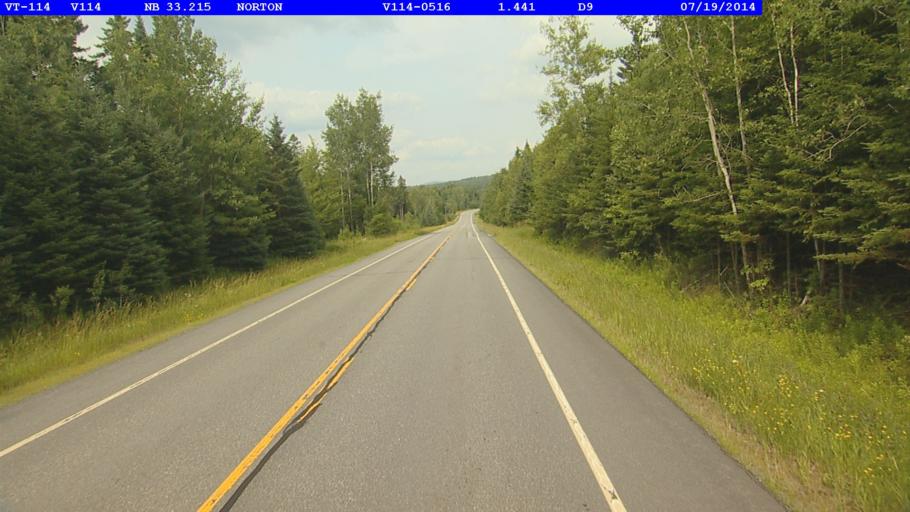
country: CA
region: Quebec
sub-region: Estrie
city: Coaticook
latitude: 44.9613
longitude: -71.8291
